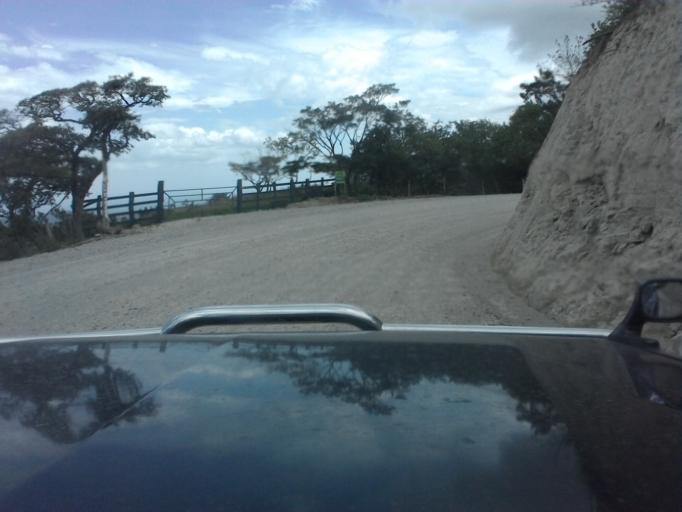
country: CR
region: Guanacaste
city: Juntas
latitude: 10.2742
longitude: -84.8411
